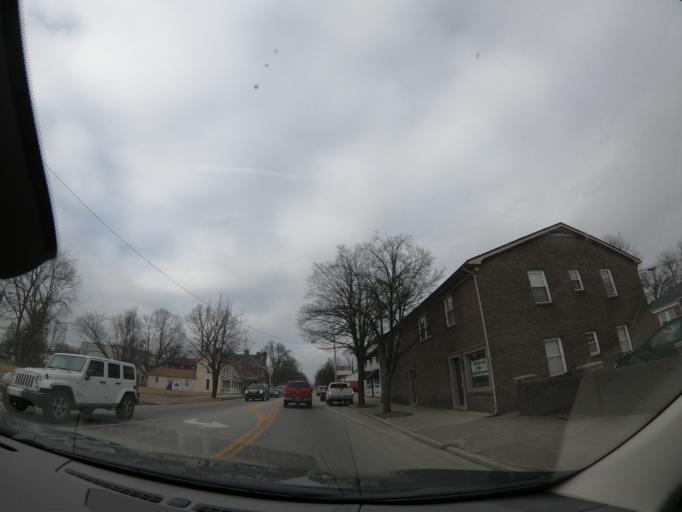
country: US
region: Kentucky
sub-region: Nelson County
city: Bardstown
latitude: 37.8121
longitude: -85.4659
